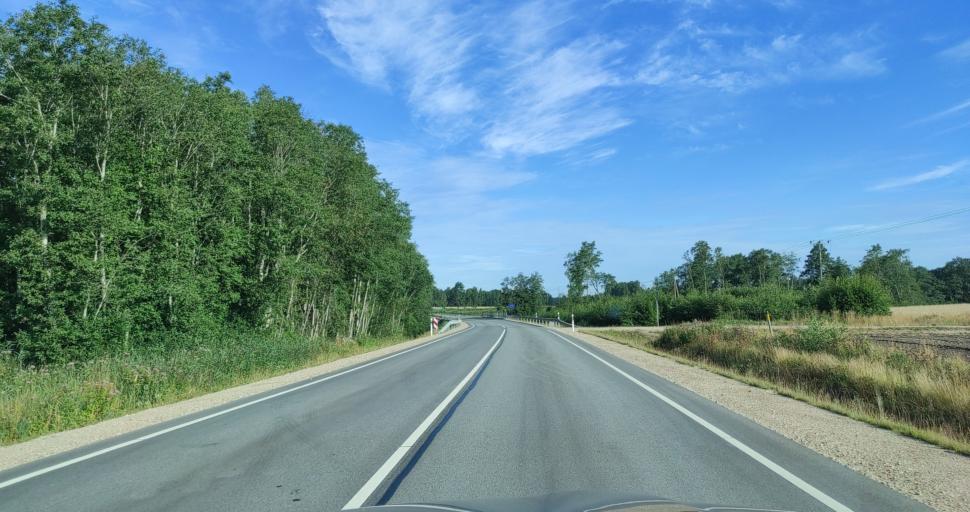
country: LV
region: Pavilostas
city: Pavilosta
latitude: 56.8310
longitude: 21.2221
